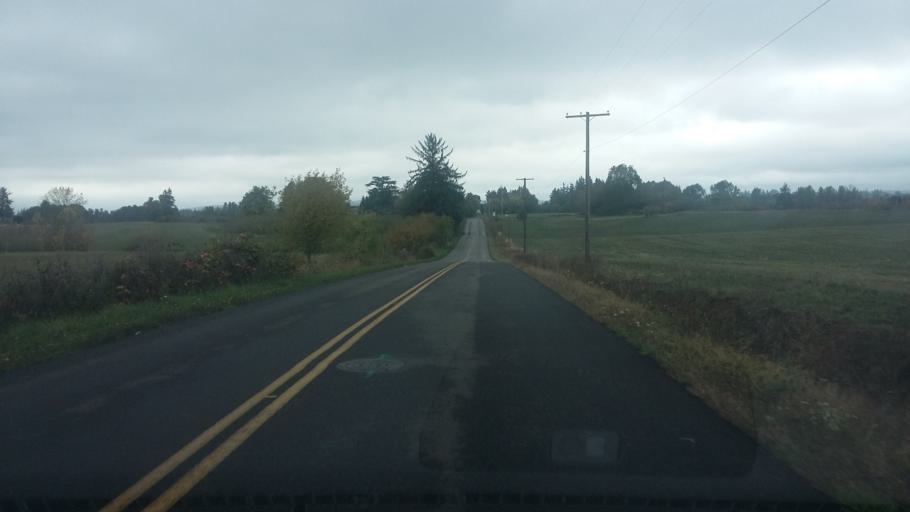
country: US
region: Washington
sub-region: Clark County
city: La Center
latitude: 45.8184
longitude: -122.6824
